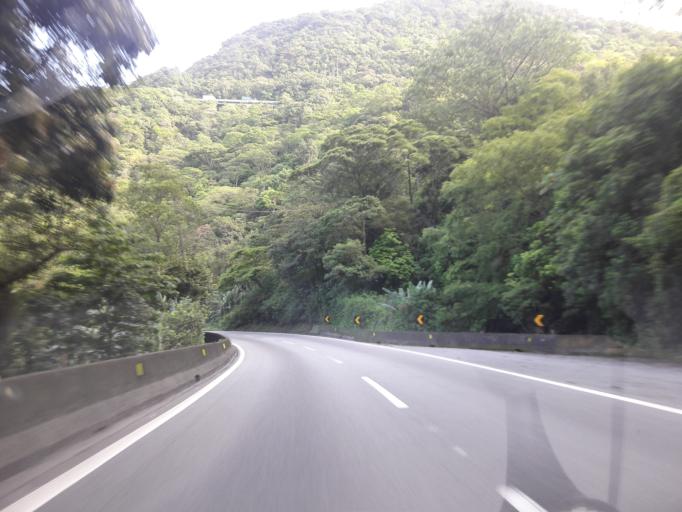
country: BR
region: Sao Paulo
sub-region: Cubatao
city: Cubatao
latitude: -23.8904
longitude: -46.4851
